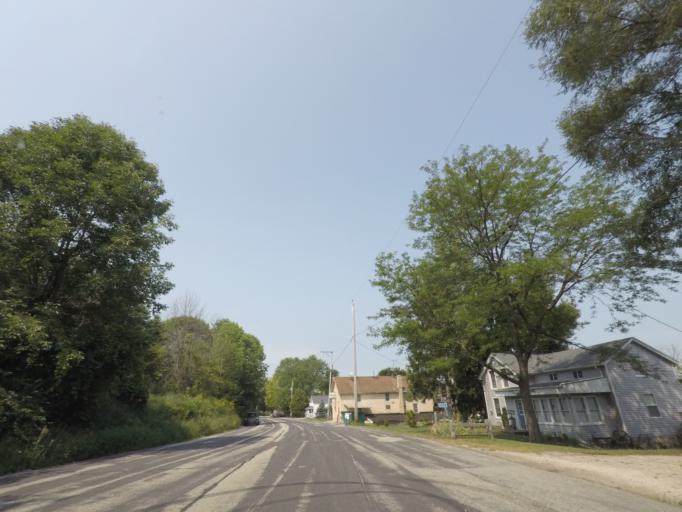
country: US
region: Wisconsin
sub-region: Jefferson County
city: Ixonia
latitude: 43.0690
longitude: -88.5965
